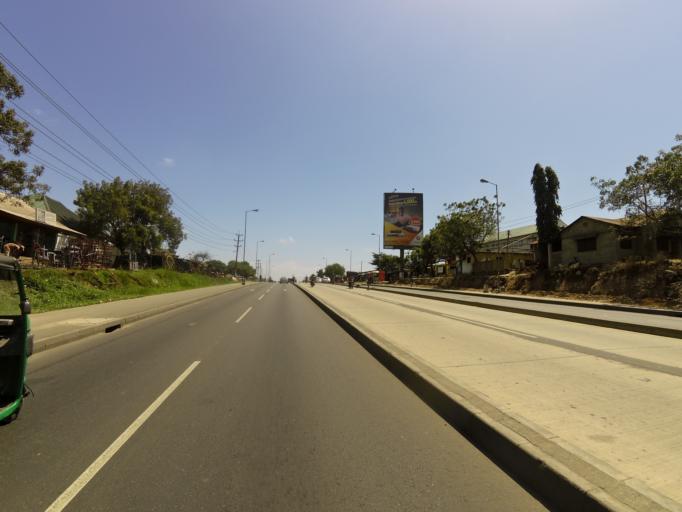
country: TZ
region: Dar es Salaam
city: Magomeni
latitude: -6.7982
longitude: 39.2632
